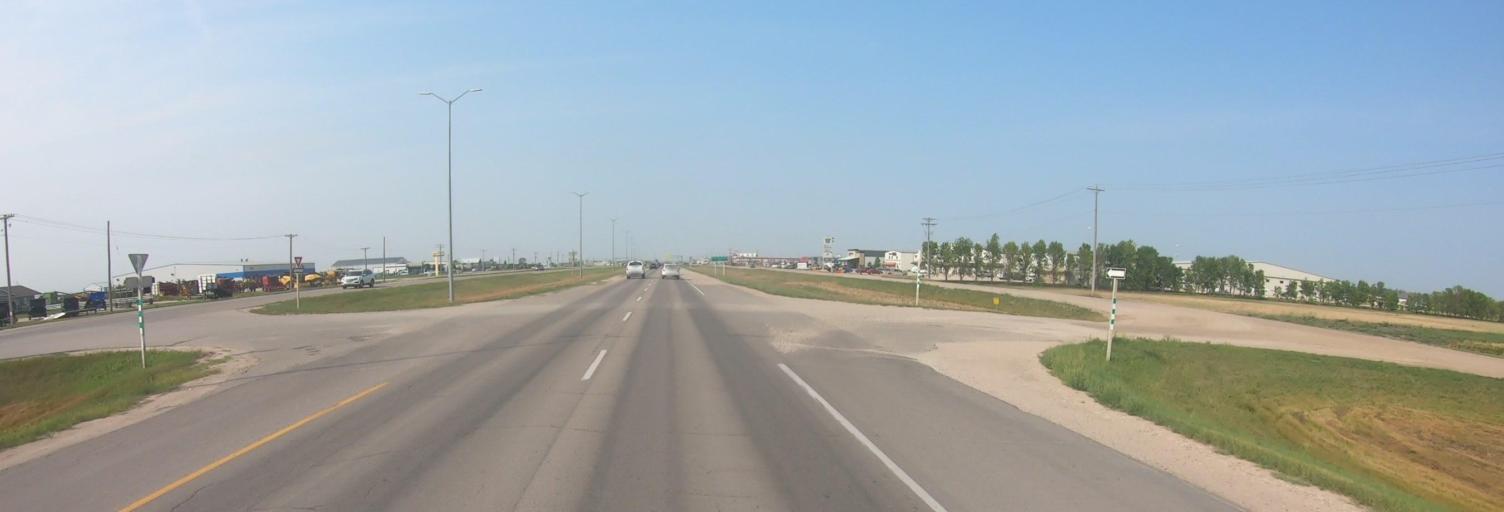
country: CA
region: Manitoba
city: Steinbach
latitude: 49.5534
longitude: -96.6880
